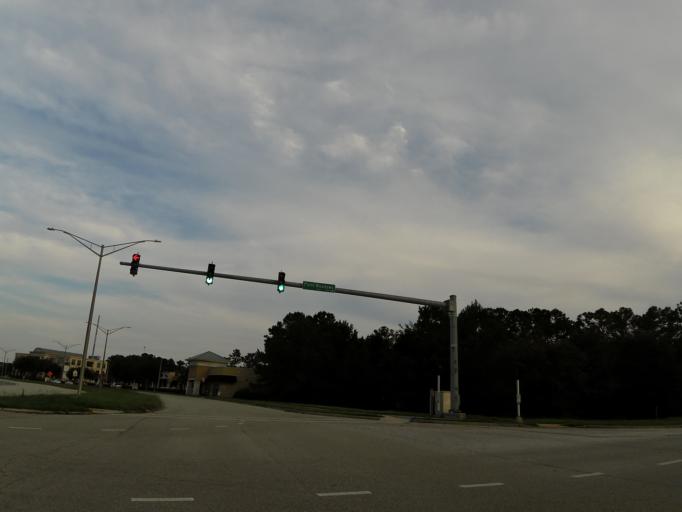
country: US
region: Florida
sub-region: Saint Johns County
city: Ponte Vedra Beach
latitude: 30.2367
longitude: -81.5190
